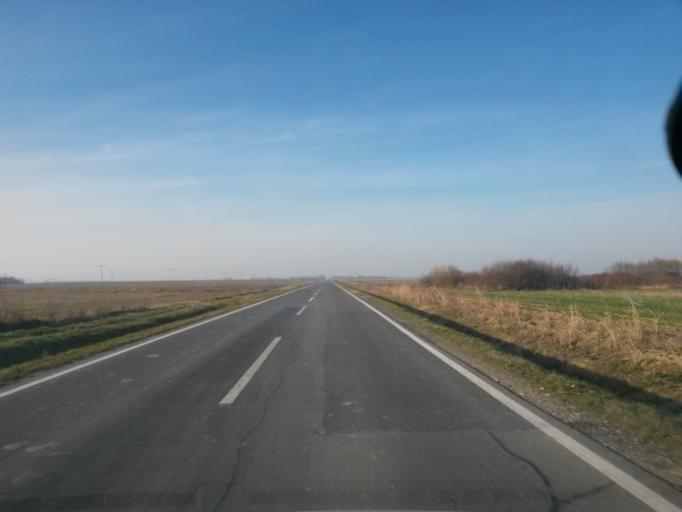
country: HR
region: Osjecko-Baranjska
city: Laslovo
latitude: 45.4218
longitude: 18.6858
